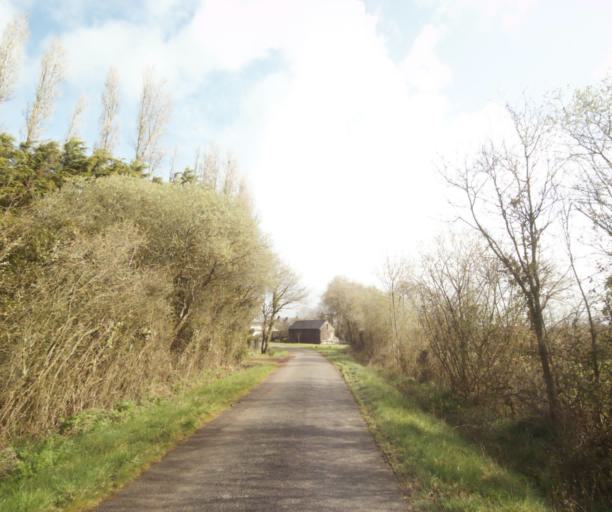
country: FR
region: Pays de la Loire
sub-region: Departement de la Loire-Atlantique
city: Bouvron
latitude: 47.4174
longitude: -1.8660
